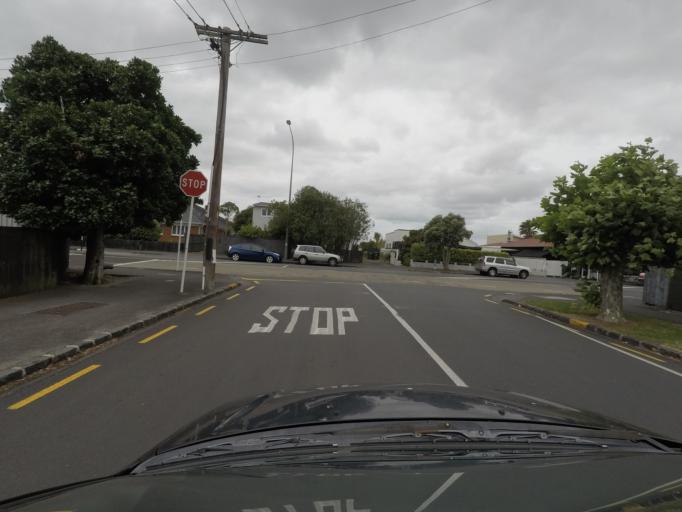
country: NZ
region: Auckland
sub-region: Auckland
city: Rosebank
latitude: -36.8649
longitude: 174.7058
